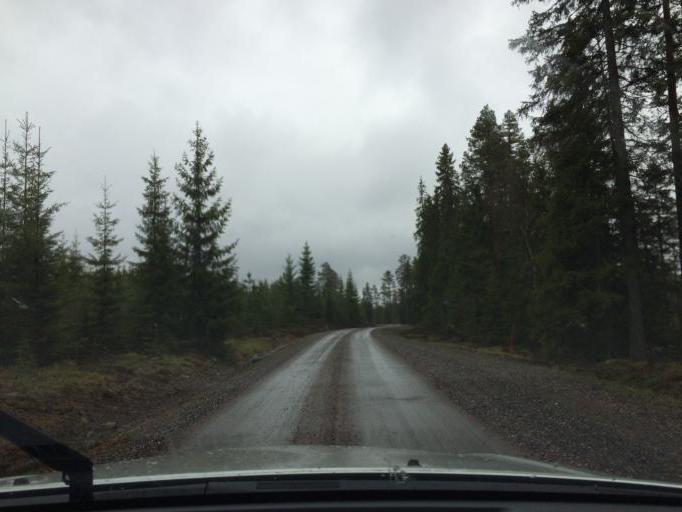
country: SE
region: OErebro
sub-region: Hallefors Kommun
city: Haellefors
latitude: 60.0252
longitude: 14.5596
